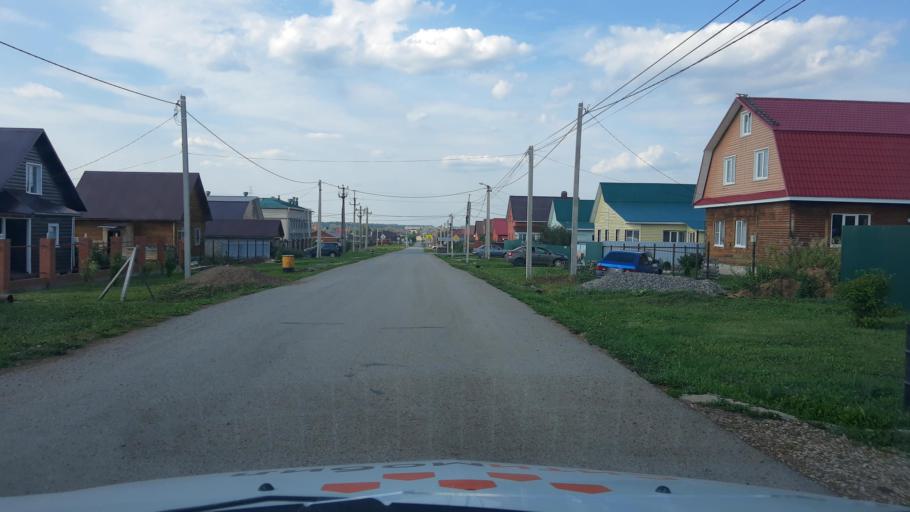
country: RU
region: Bashkortostan
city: Kabakovo
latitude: 54.6543
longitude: 56.2125
